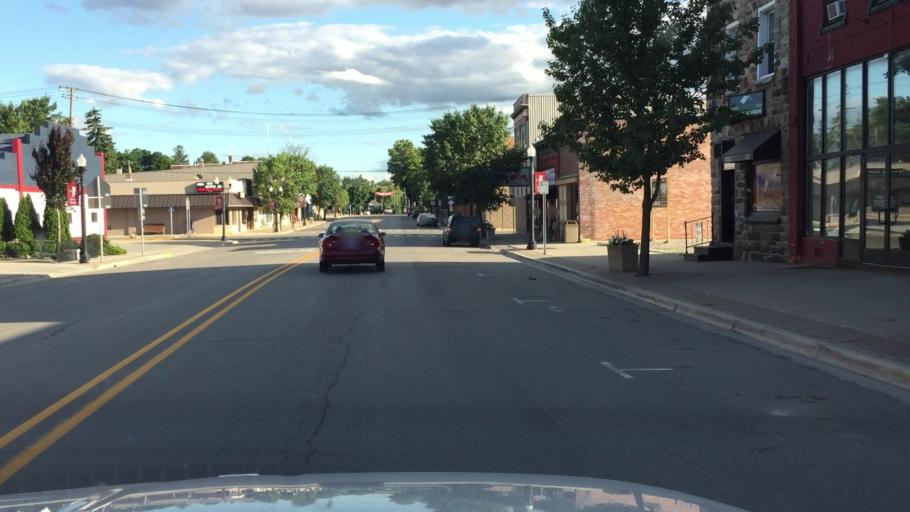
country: US
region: Michigan
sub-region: Saint Clair County
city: Yale
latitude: 43.1296
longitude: -82.7984
